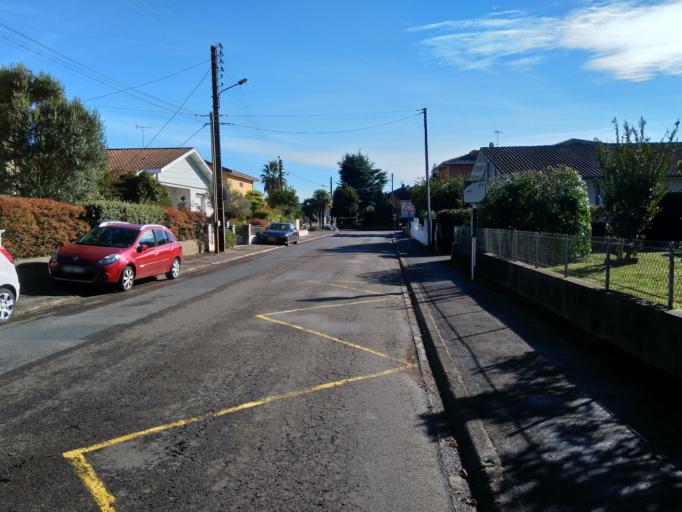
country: FR
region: Aquitaine
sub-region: Departement des Landes
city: Saint-Paul-les-Dax
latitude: 43.7293
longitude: -1.0527
